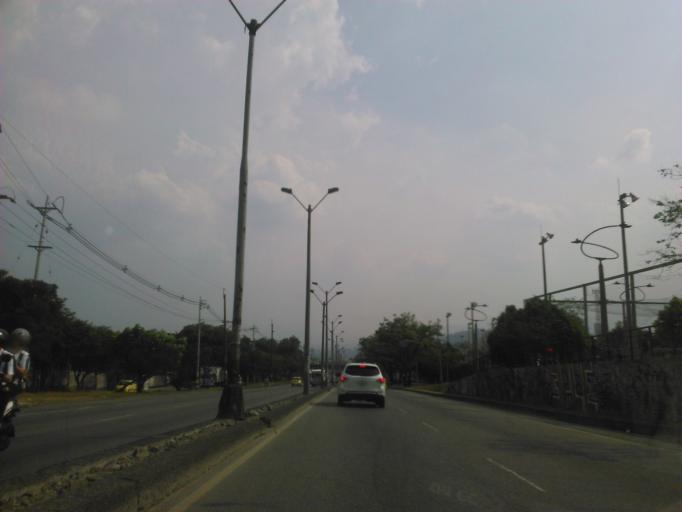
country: CO
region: Antioquia
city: Medellin
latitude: 6.2946
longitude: -75.5676
